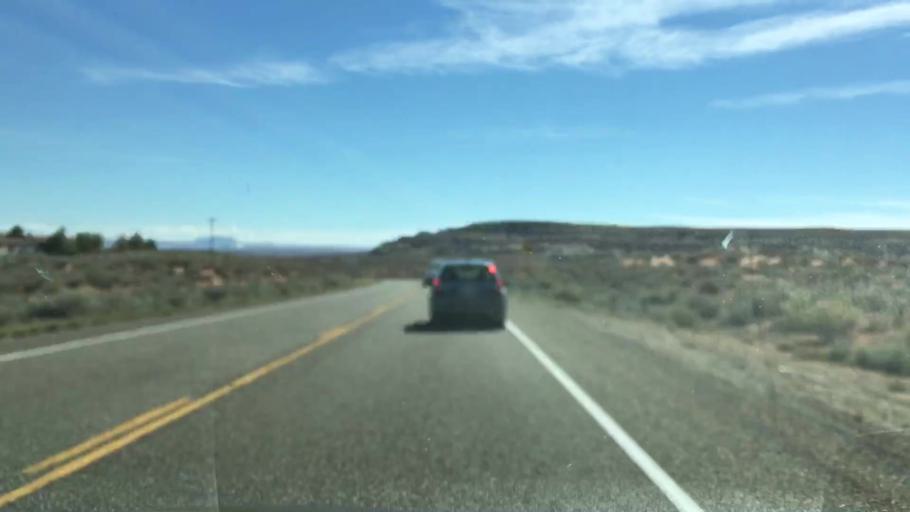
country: US
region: Arizona
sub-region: Coconino County
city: Page
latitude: 37.0584
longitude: -111.6403
